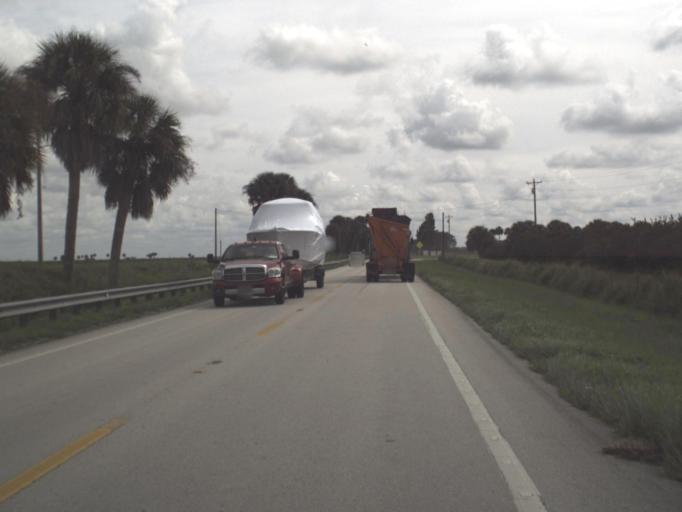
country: US
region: Florida
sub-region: Highlands County
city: Lake Placid
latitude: 27.2090
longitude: -81.2155
